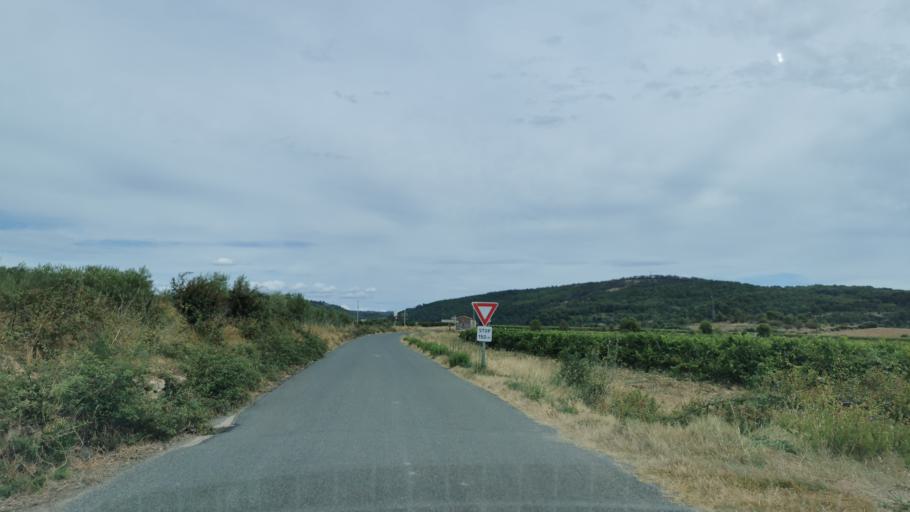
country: FR
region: Languedoc-Roussillon
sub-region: Departement de l'Aude
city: Bize-Minervois
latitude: 43.3103
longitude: 2.8561
